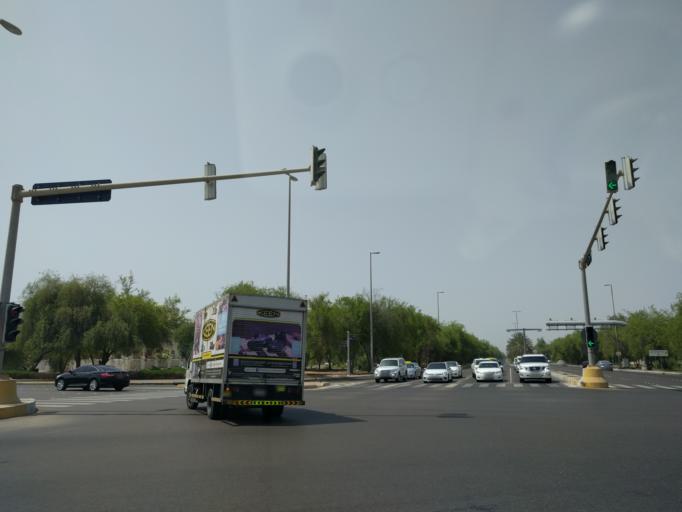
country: AE
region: Abu Dhabi
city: Abu Dhabi
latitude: 24.4340
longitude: 54.4300
